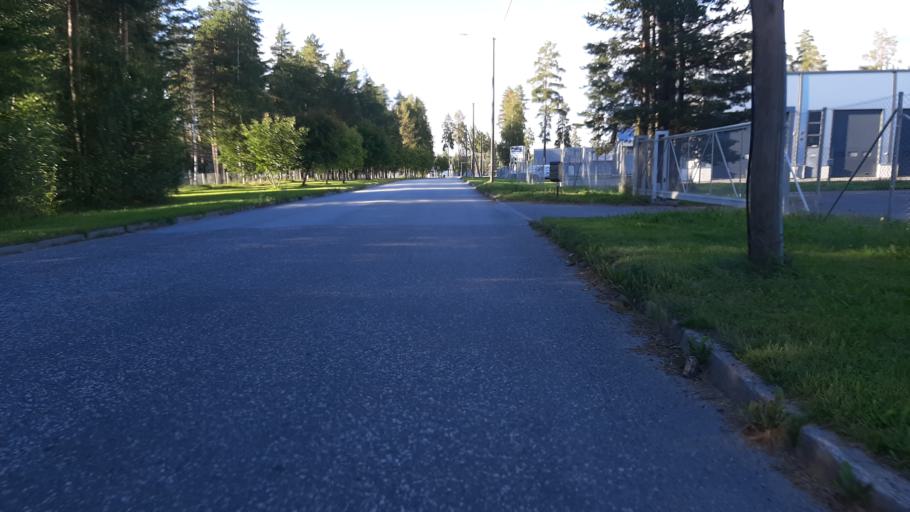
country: FI
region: North Karelia
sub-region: Joensuu
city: Joensuu
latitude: 62.6258
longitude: 29.7712
